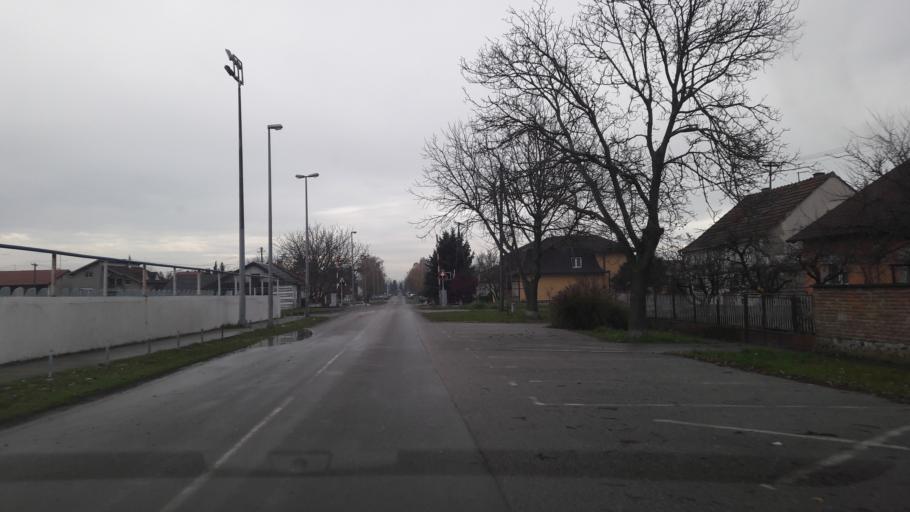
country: HR
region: Osjecko-Baranjska
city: Visnjevac
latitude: 45.5611
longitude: 18.6185
